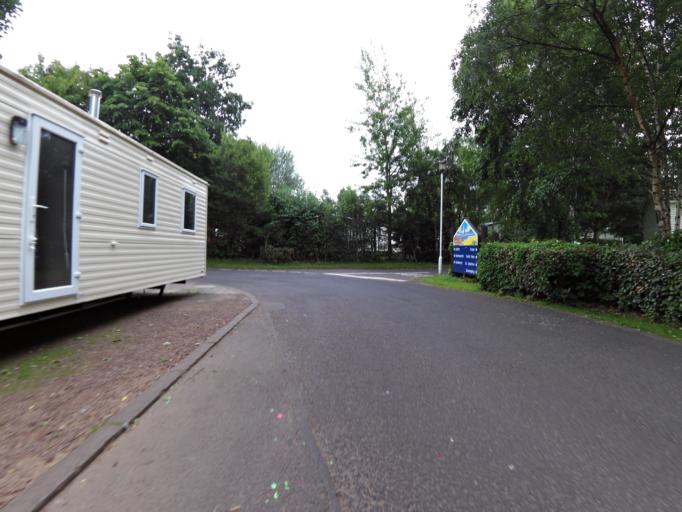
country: GB
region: Scotland
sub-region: East Lothian
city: Cockenzie
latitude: 55.9712
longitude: -2.9324
